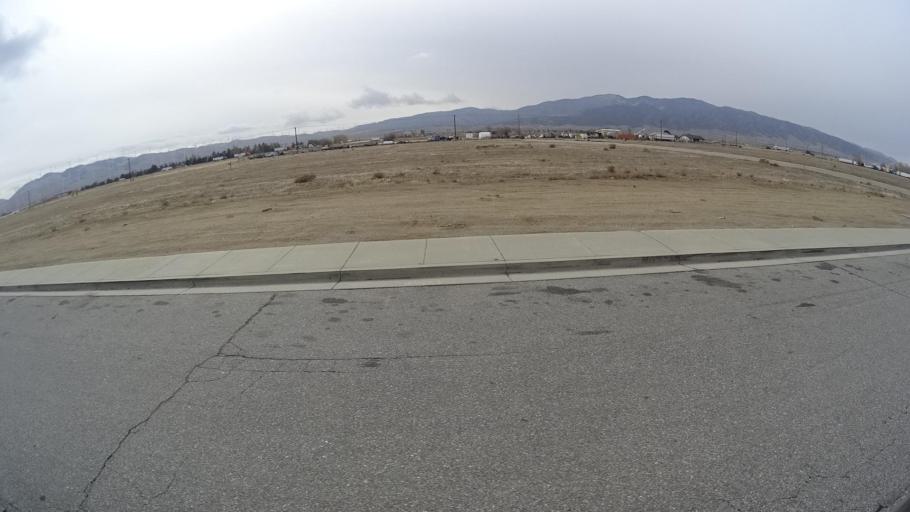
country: US
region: California
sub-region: Kern County
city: Tehachapi
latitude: 35.1262
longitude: -118.4030
